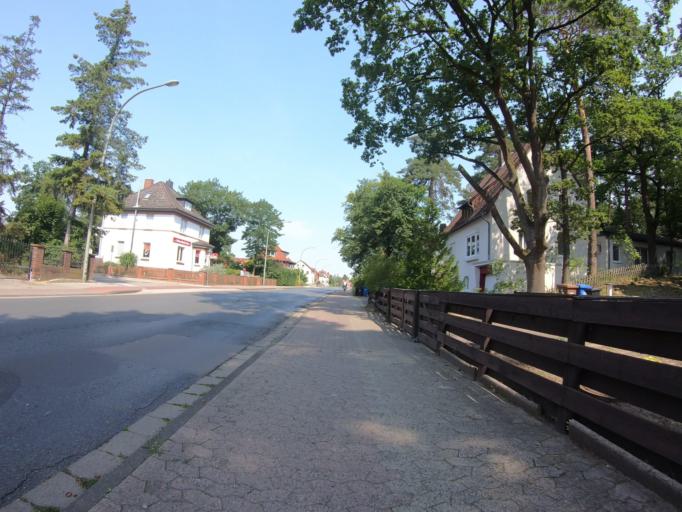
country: DE
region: Lower Saxony
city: Gifhorn
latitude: 52.4778
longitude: 10.5535
